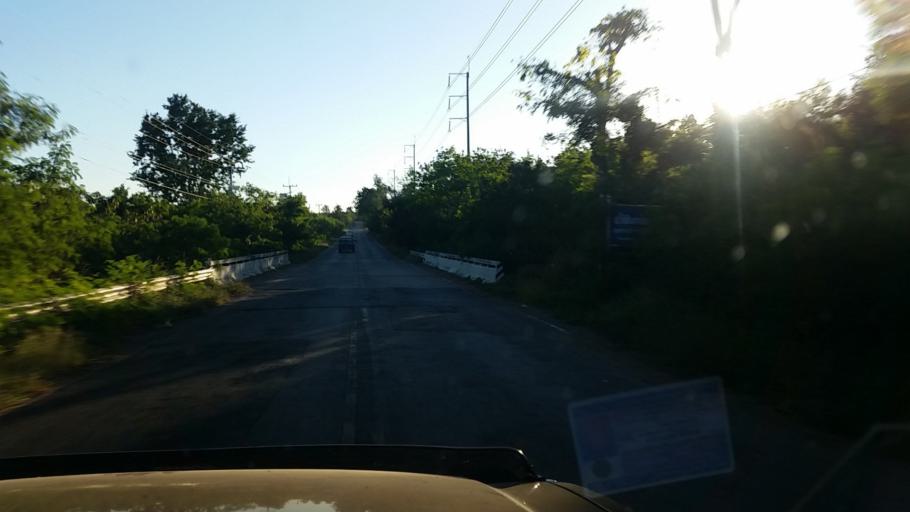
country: TH
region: Chaiyaphum
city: Nong Bua Rawe
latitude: 15.6882
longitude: 101.7046
